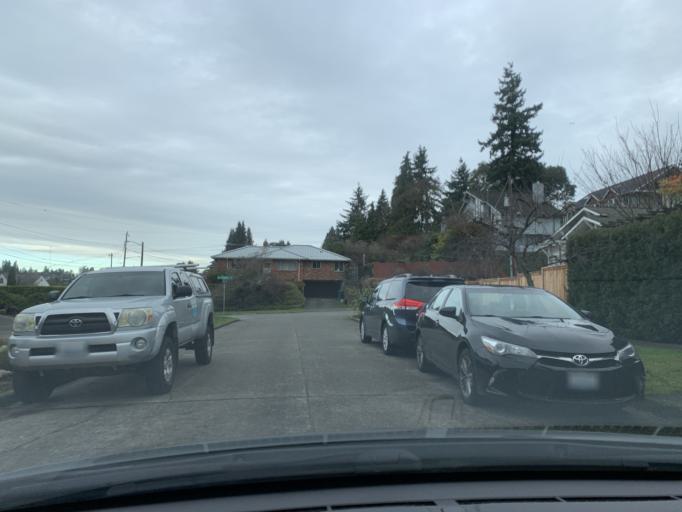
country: US
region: Washington
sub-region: King County
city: White Center
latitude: 47.5563
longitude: -122.3897
